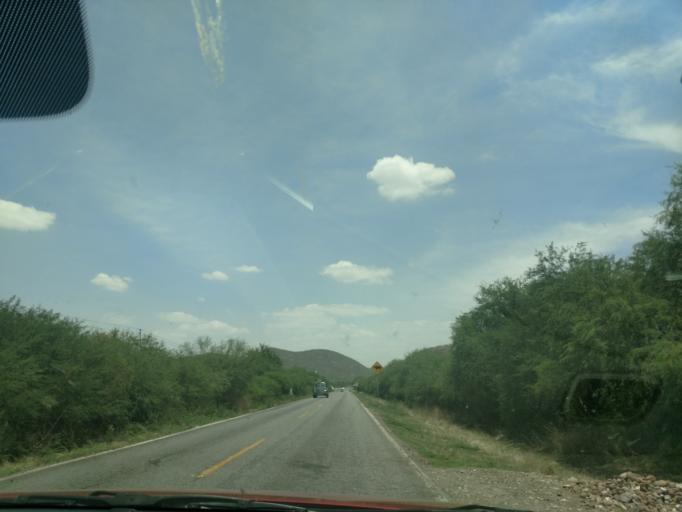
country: MX
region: San Luis Potosi
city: Ciudad Fernandez
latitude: 22.0080
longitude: -100.1519
